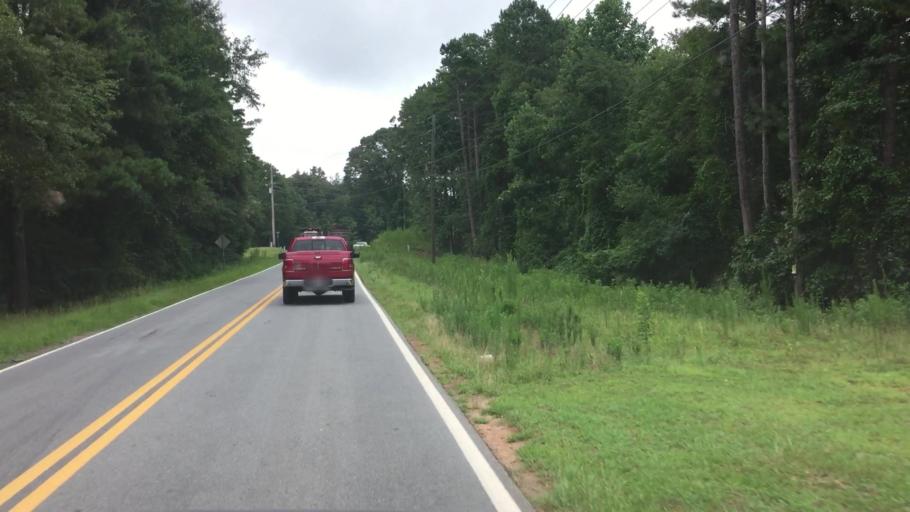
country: US
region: Georgia
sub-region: Barrow County
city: Winder
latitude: 34.0340
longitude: -83.7196
